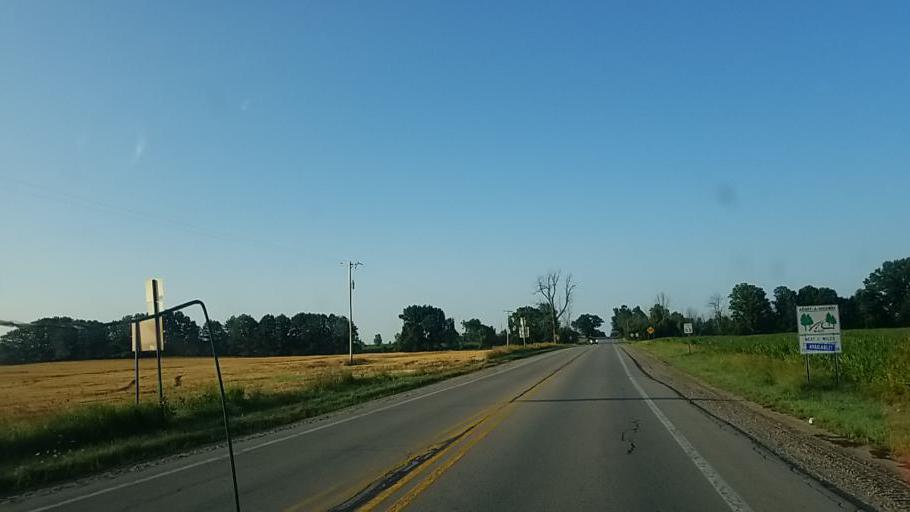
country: US
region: Michigan
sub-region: Montcalm County
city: Lakeview
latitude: 43.4302
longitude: -85.2633
